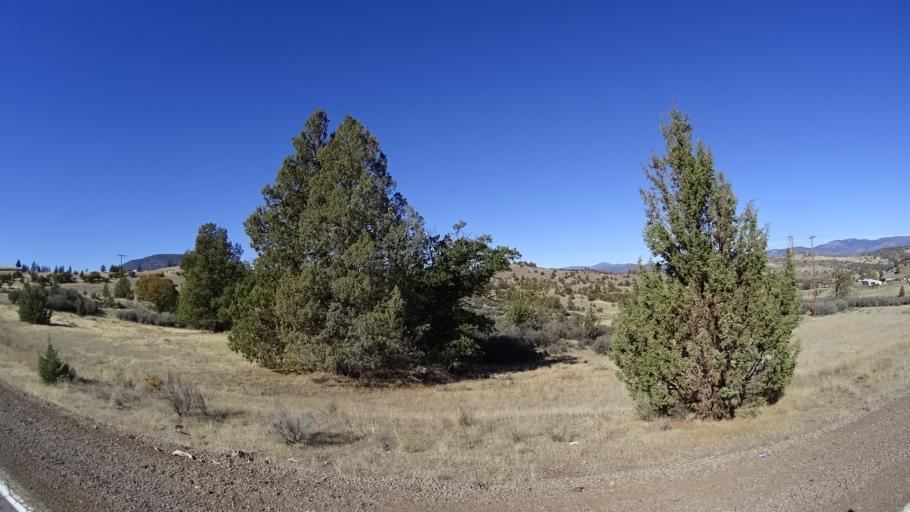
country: US
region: California
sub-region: Siskiyou County
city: Montague
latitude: 41.8742
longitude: -122.4220
